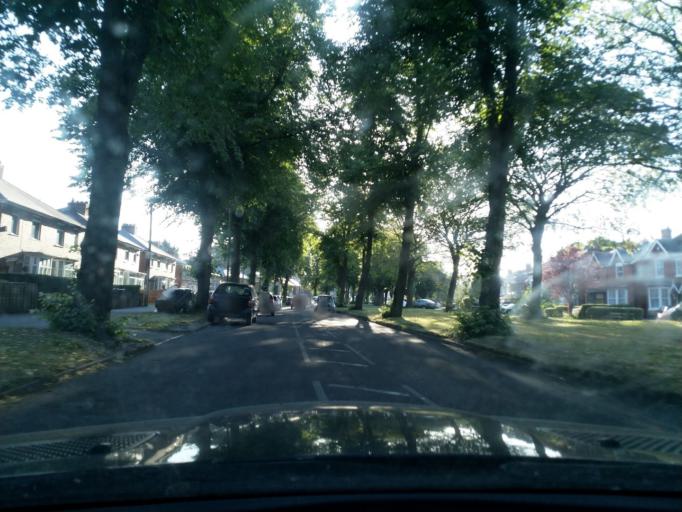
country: GB
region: England
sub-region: City and Borough of Birmingham
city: Acocks Green
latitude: 52.4422
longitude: -1.8298
